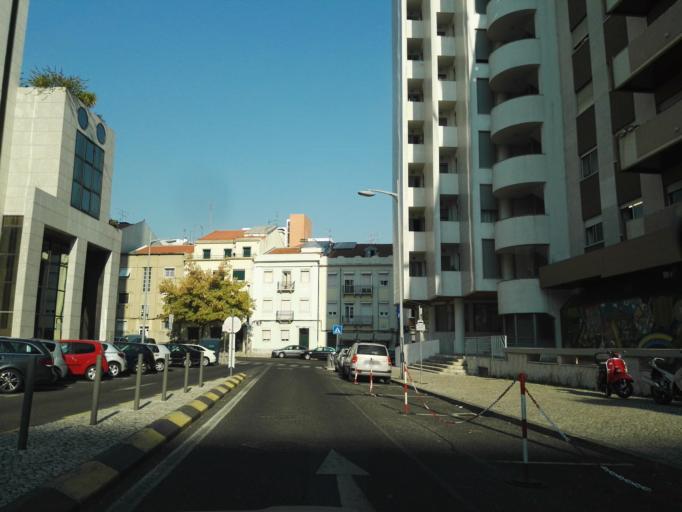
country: PT
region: Lisbon
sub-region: Lisbon
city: Lisbon
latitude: 38.7453
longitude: -9.1593
